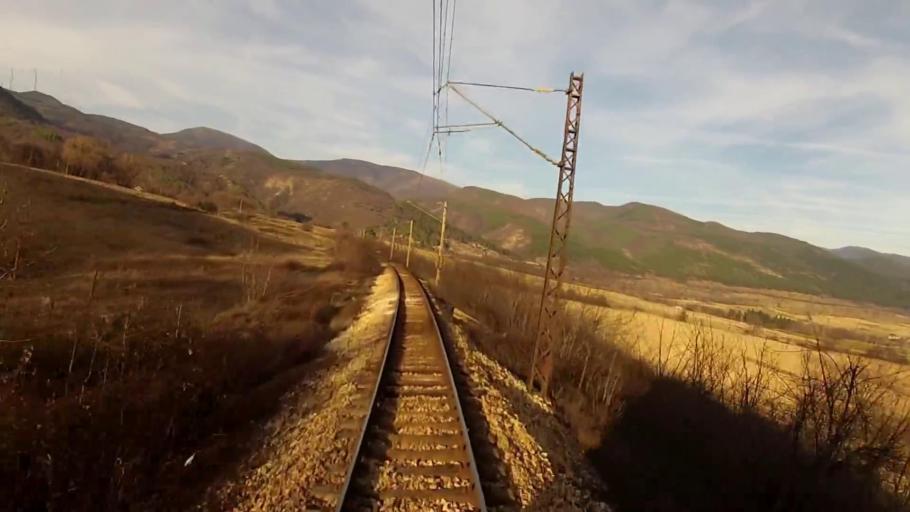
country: BG
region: Plovdiv
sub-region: Obshtina Karlovo
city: Klisura
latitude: 42.7145
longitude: 24.5522
